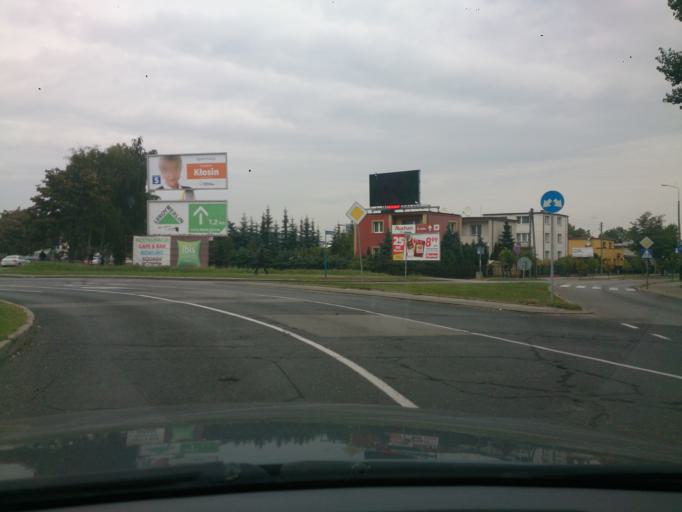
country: PL
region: Pomeranian Voivodeship
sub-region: Powiat wejherowski
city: Rumia
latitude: 54.5712
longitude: 18.3881
